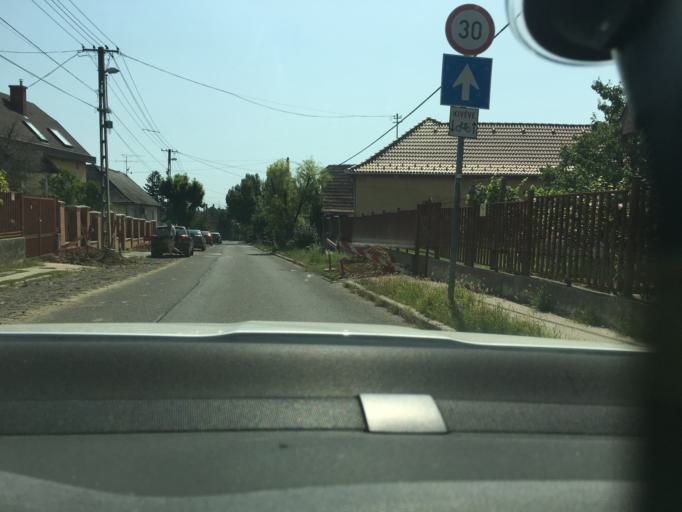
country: HU
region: Pest
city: Csomor
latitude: 47.5198
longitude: 19.2268
